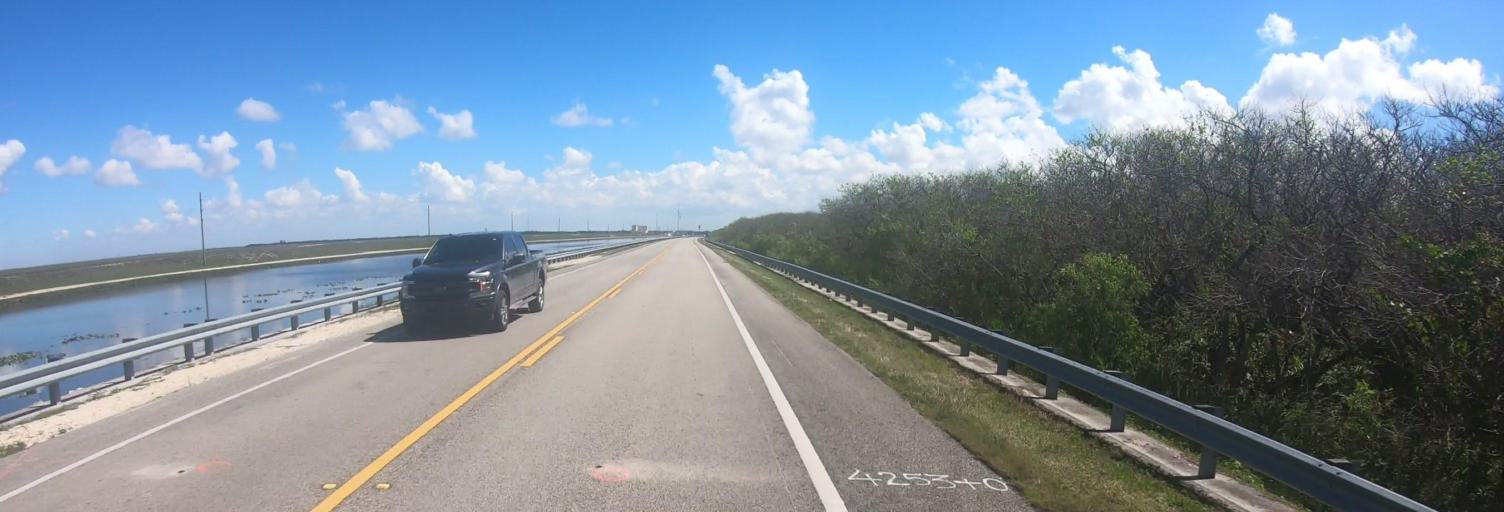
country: US
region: Florida
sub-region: Miami-Dade County
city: Kendall West
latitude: 25.7602
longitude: -80.5158
